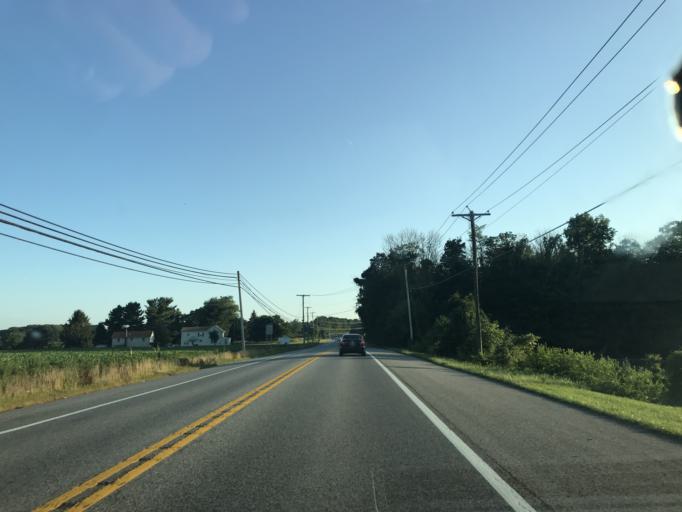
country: US
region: Maryland
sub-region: Harford County
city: South Bel Air
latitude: 39.5911
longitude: -76.3243
